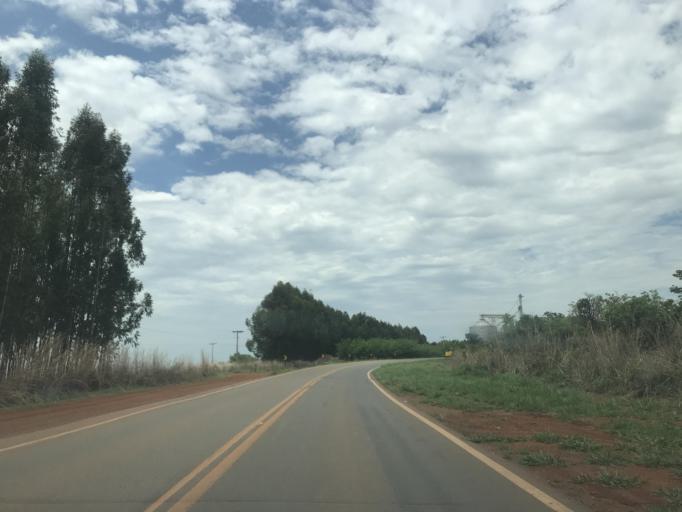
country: BR
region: Goias
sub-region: Luziania
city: Luziania
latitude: -16.3426
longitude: -48.0184
